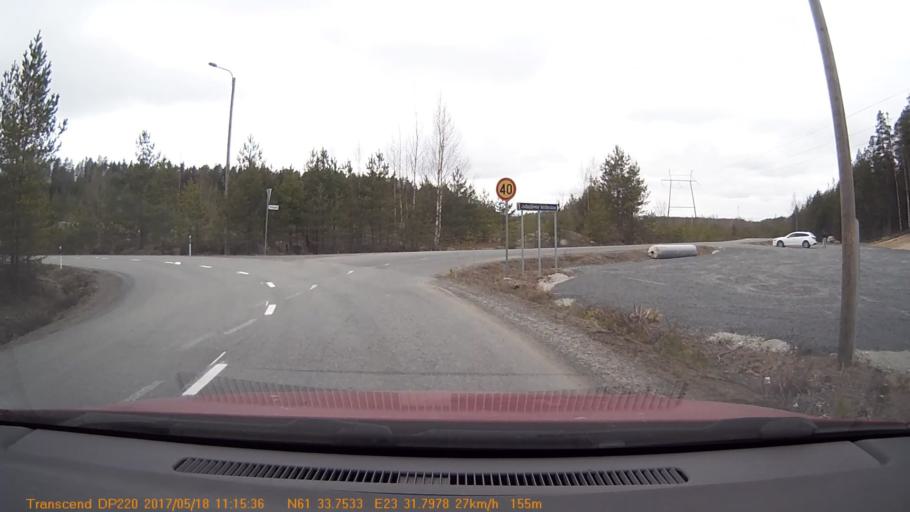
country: FI
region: Pirkanmaa
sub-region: Tampere
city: Yloejaervi
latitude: 61.5626
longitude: 23.5301
